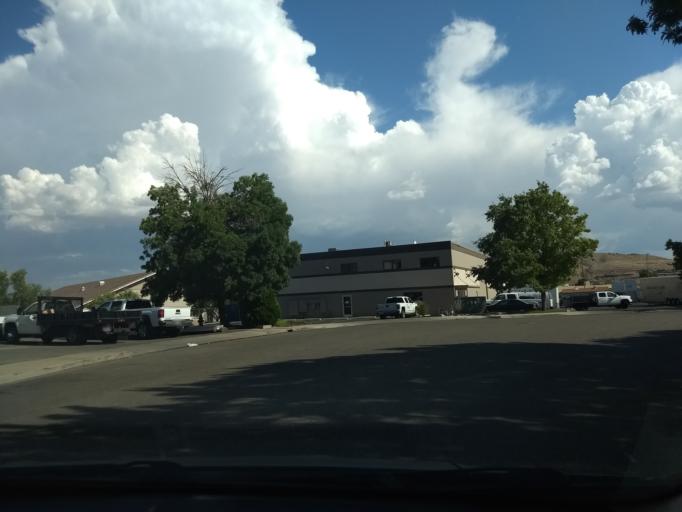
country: US
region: Utah
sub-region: Washington County
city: Saint George
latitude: 37.0847
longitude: -113.5769
